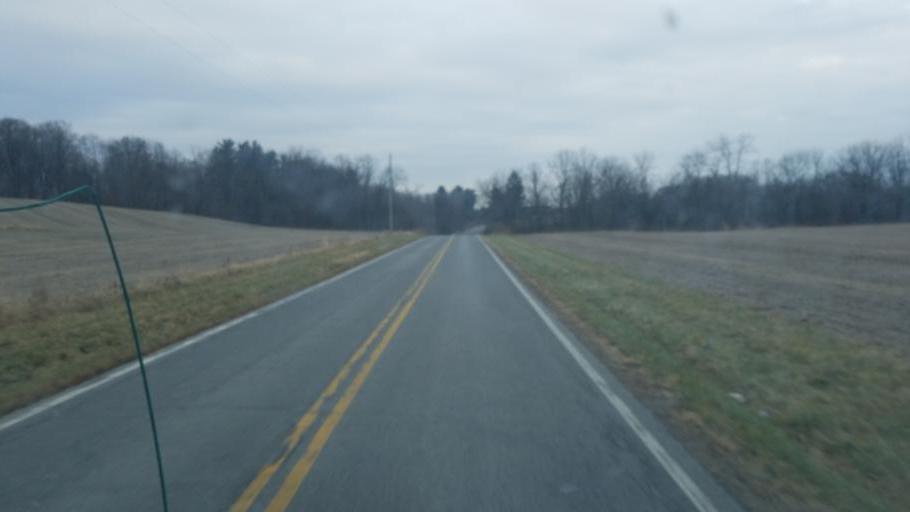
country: US
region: Ohio
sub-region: Delaware County
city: Ashley
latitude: 40.3478
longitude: -82.9476
